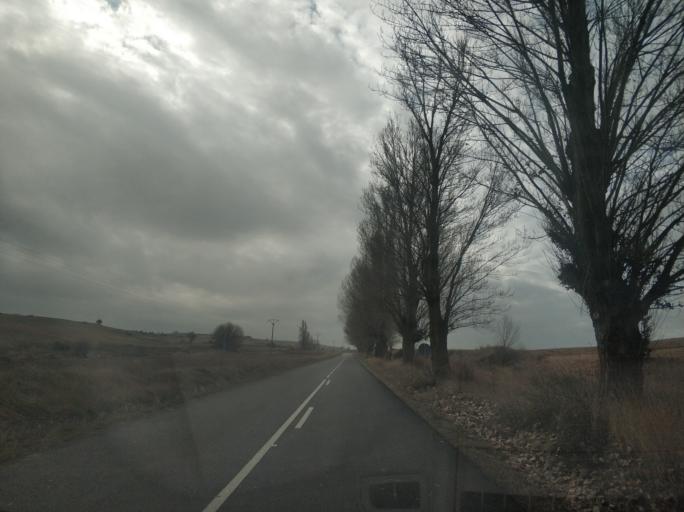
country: ES
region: Castille and Leon
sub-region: Provincia de Burgos
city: Penaranda de Duero
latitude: 41.6767
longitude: -3.4797
